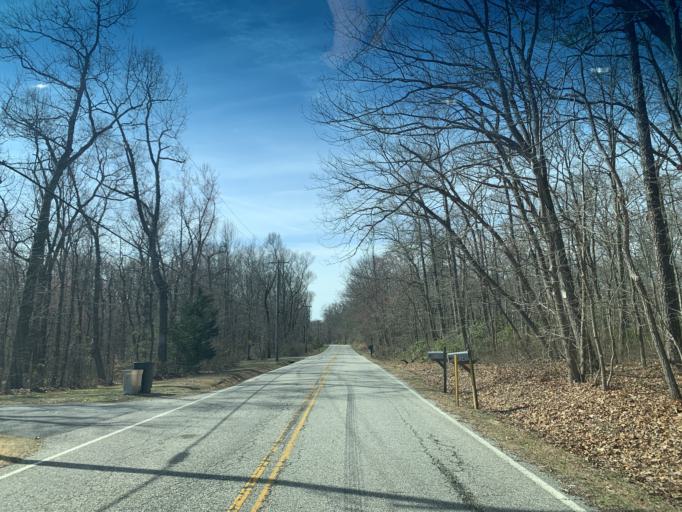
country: US
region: Maryland
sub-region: Cecil County
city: Charlestown
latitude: 39.5738
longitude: -75.9871
